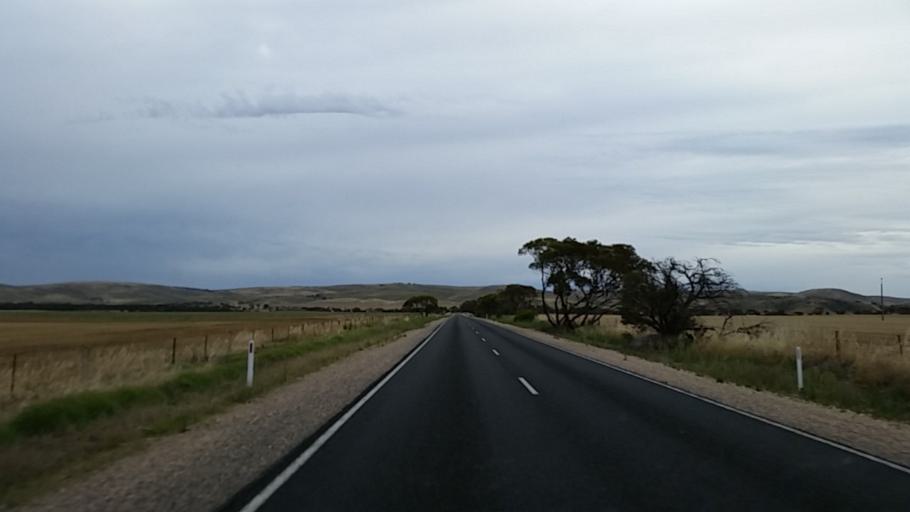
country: AU
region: South Australia
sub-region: Mid Murray
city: Mannum
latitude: -34.7555
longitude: 139.2339
